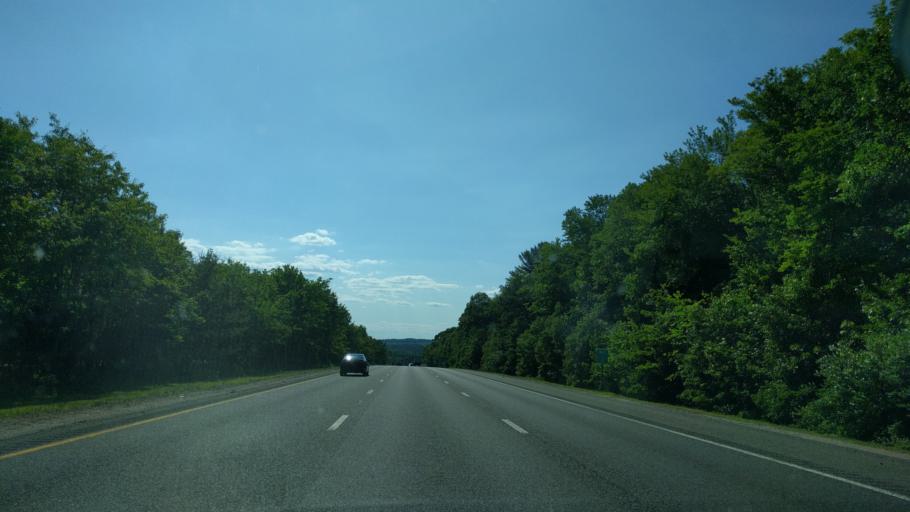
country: US
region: Rhode Island
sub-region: Providence County
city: Valley Falls
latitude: 41.9500
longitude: -71.3581
